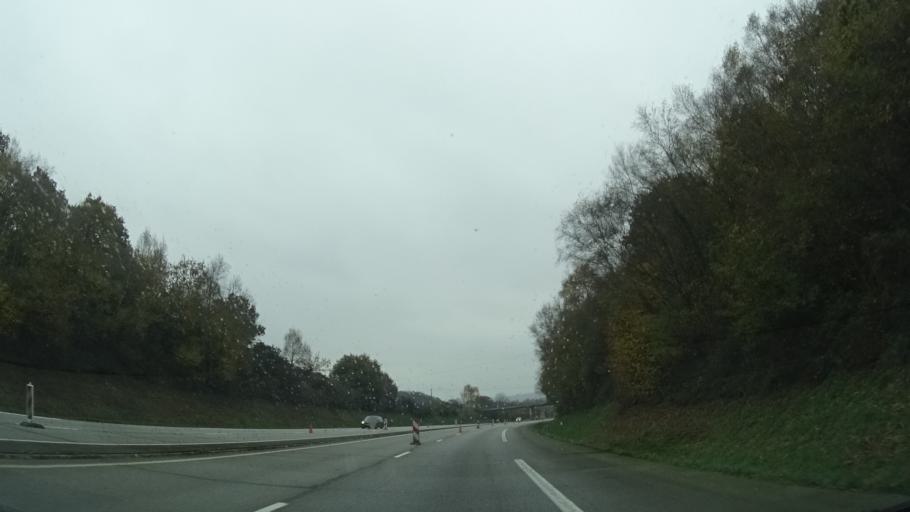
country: FR
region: Brittany
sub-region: Departement du Finistere
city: Dineault
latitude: 48.2626
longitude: -4.1132
